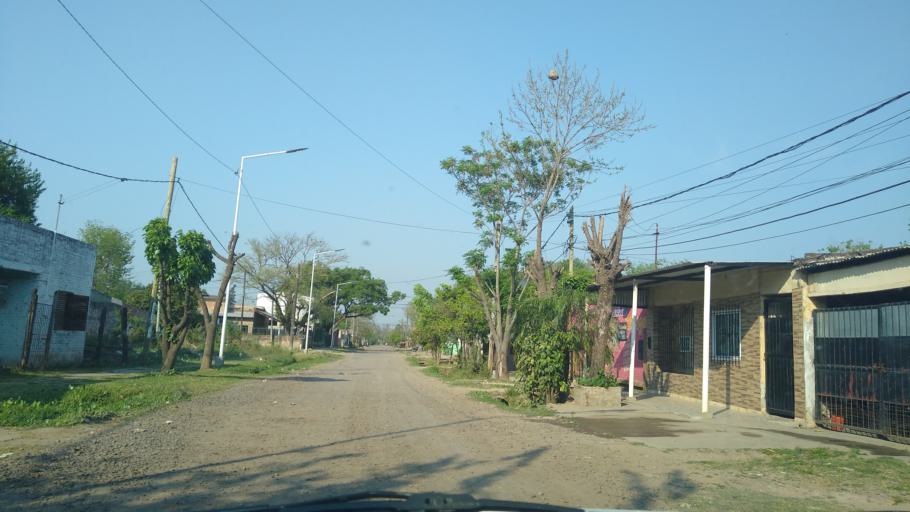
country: AR
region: Chaco
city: Barranqueras
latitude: -27.4740
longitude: -58.9479
